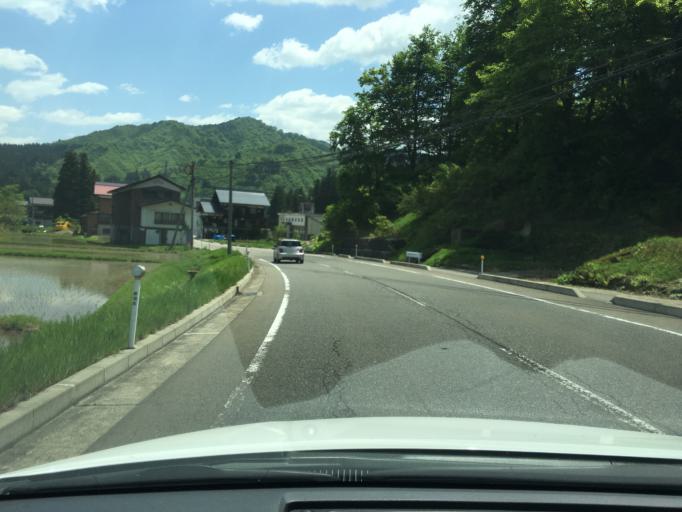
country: JP
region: Niigata
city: Tochio-honcho
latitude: 37.3508
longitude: 139.0424
